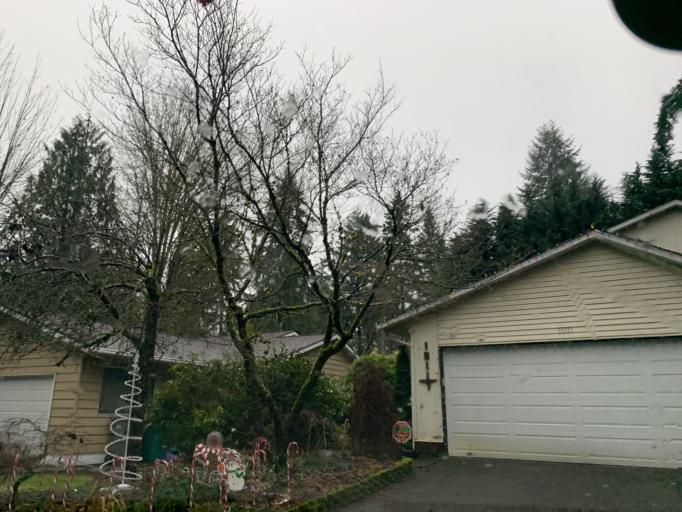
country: US
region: Washington
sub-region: King County
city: Kingsgate
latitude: 47.7379
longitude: -122.1792
